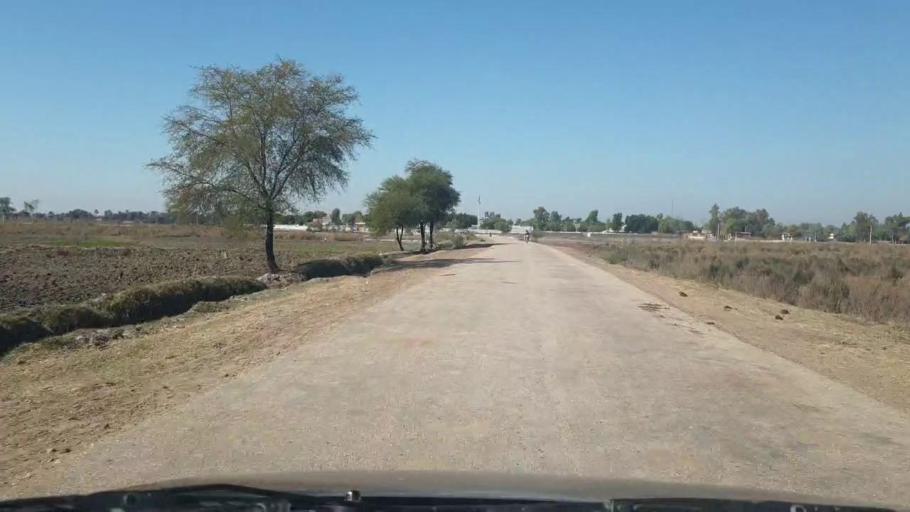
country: PK
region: Sindh
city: Bozdar
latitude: 27.1282
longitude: 68.6379
